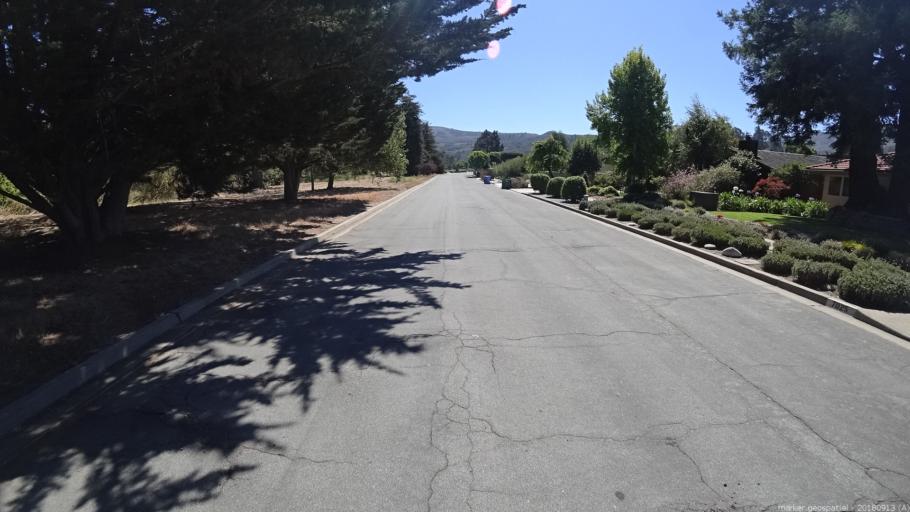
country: US
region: California
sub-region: Monterey County
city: Carmel-by-the-Sea
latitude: 36.5356
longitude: -121.8655
